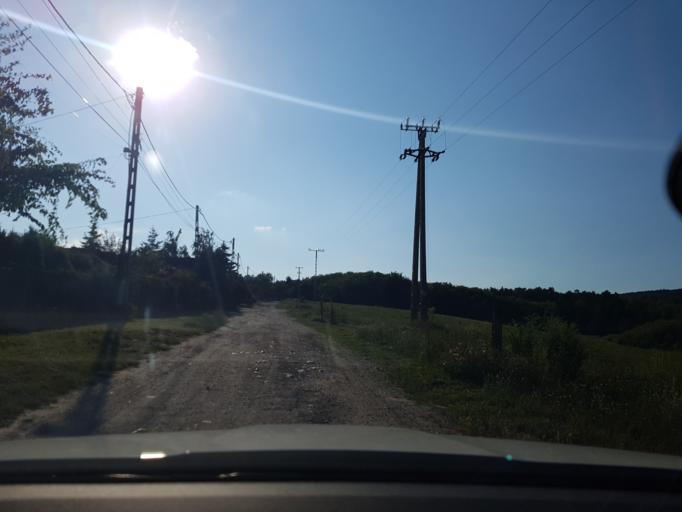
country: HU
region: Pest
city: Pilisszentivan
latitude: 47.6163
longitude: 18.8781
